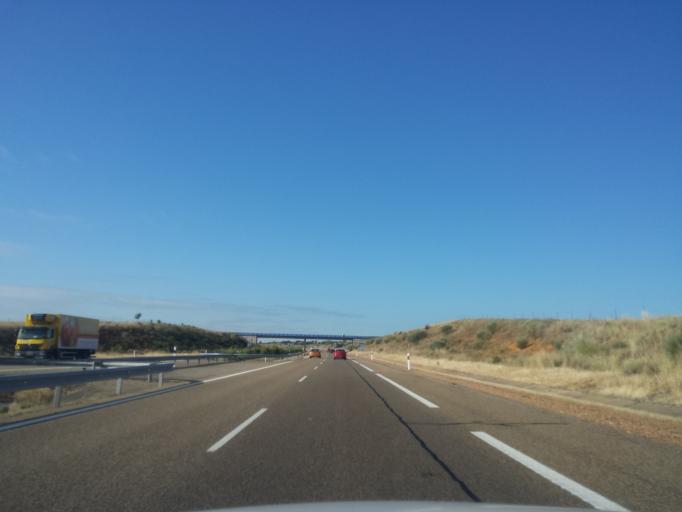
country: ES
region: Castille and Leon
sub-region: Provincia de Leon
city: Valdevimbre
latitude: 42.4071
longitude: -5.5912
